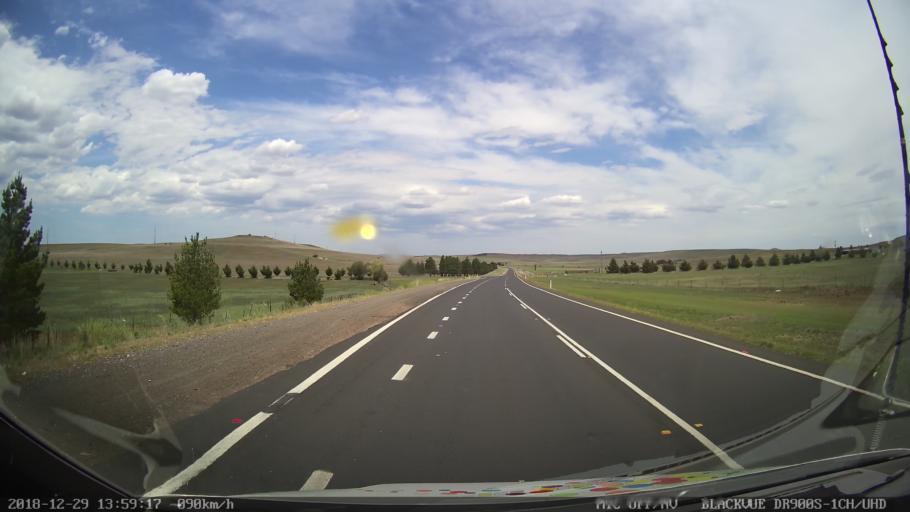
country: AU
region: New South Wales
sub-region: Cooma-Monaro
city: Cooma
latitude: -36.2505
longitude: 149.1479
